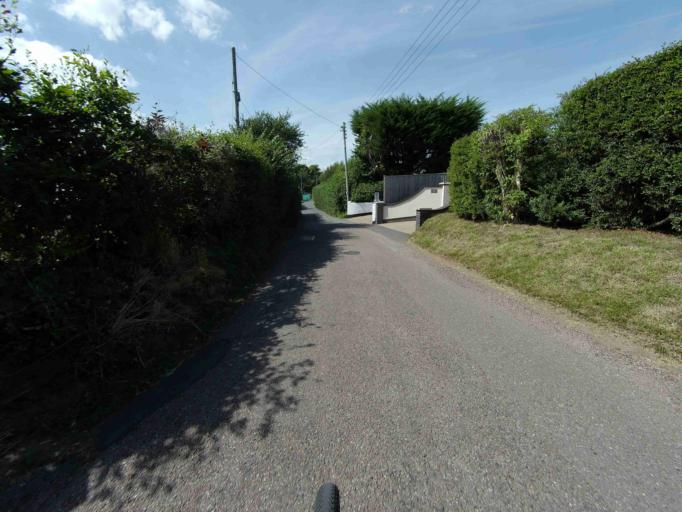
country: GB
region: England
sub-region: Devon
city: Topsham
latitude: 50.6715
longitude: -3.4431
